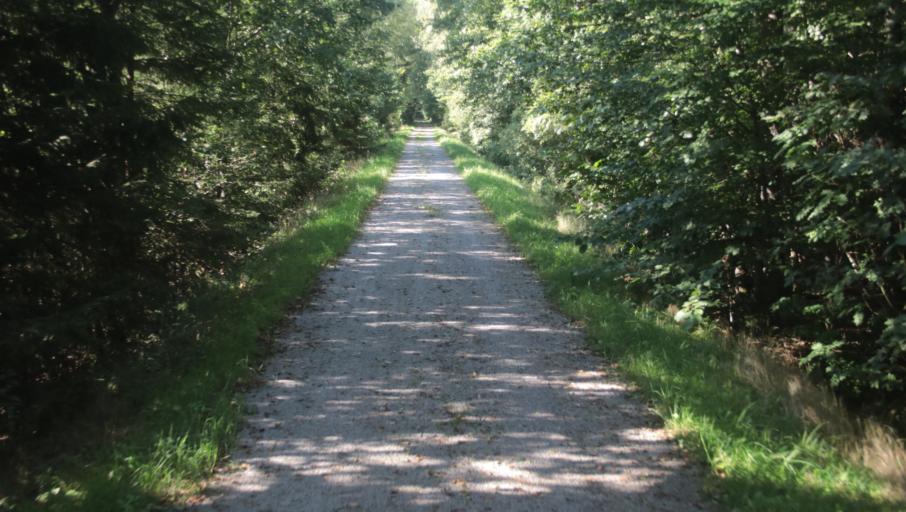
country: SE
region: Blekinge
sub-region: Karlshamns Kommun
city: Svangsta
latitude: 56.3440
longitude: 14.6957
